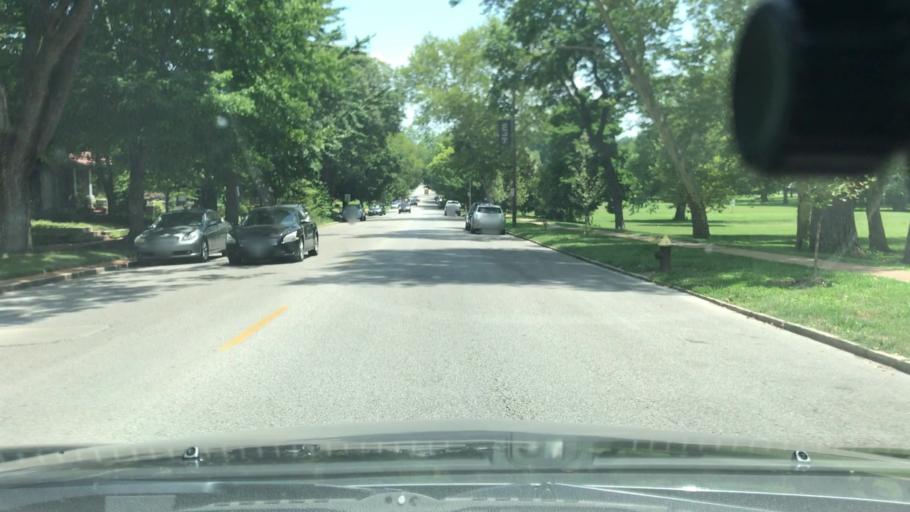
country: US
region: Missouri
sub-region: City of Saint Louis
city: St. Louis
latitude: 38.6081
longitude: -90.2511
